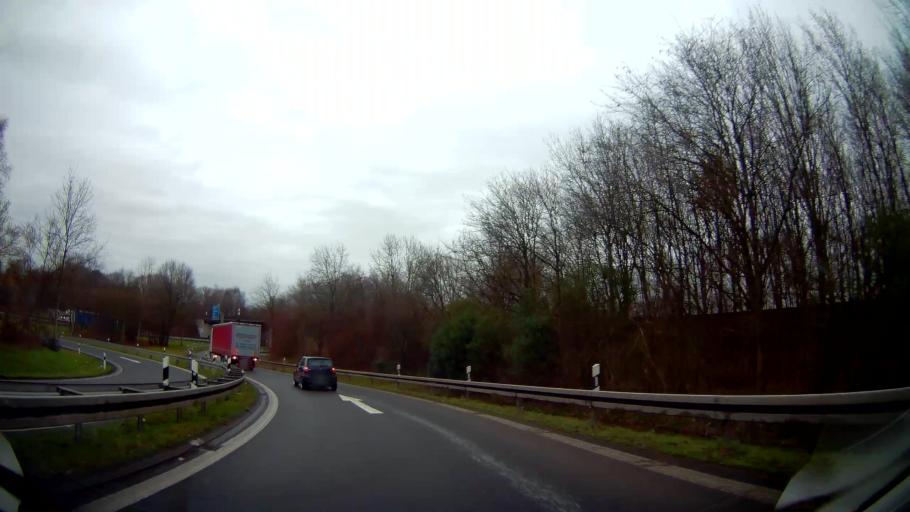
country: DE
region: North Rhine-Westphalia
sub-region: Regierungsbezirk Munster
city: Gladbeck
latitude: 51.5520
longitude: 6.9669
